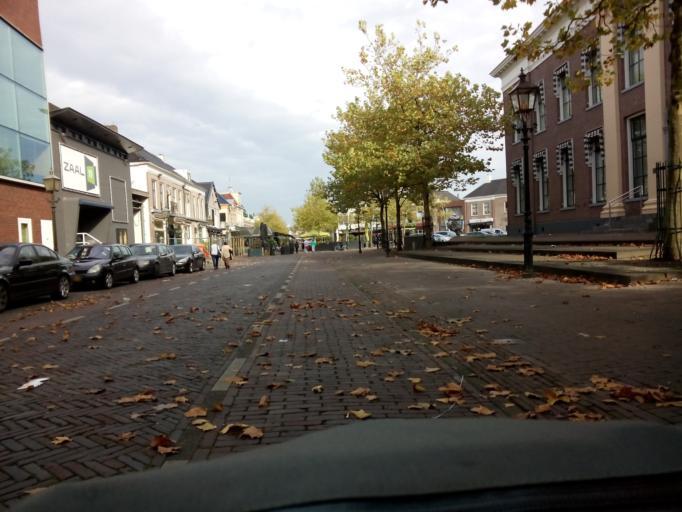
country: NL
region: Drenthe
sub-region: Gemeente Assen
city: Assen
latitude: 52.9941
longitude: 6.5637
